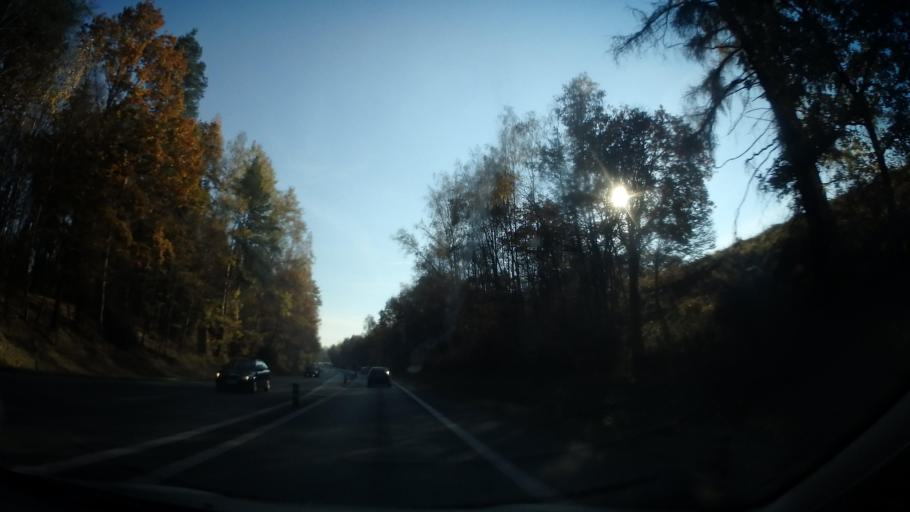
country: CZ
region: Central Bohemia
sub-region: Okres Benesov
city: Cercany
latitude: 49.8784
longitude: 14.7066
